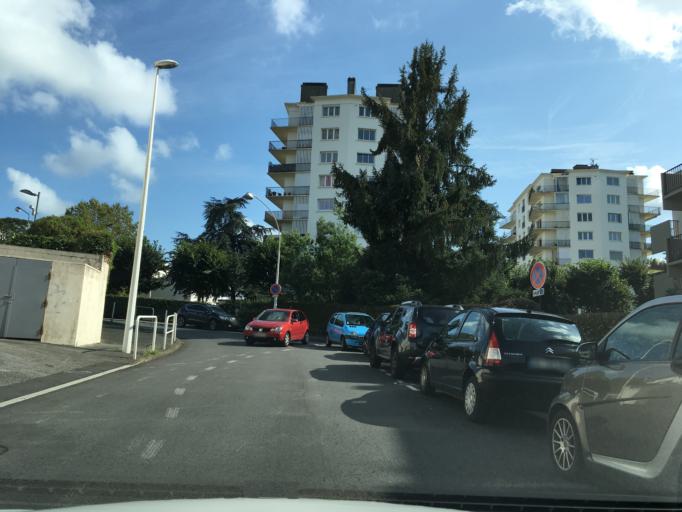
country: FR
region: Aquitaine
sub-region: Departement des Pyrenees-Atlantiques
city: Bayonne
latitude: 43.4792
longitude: -1.4856
